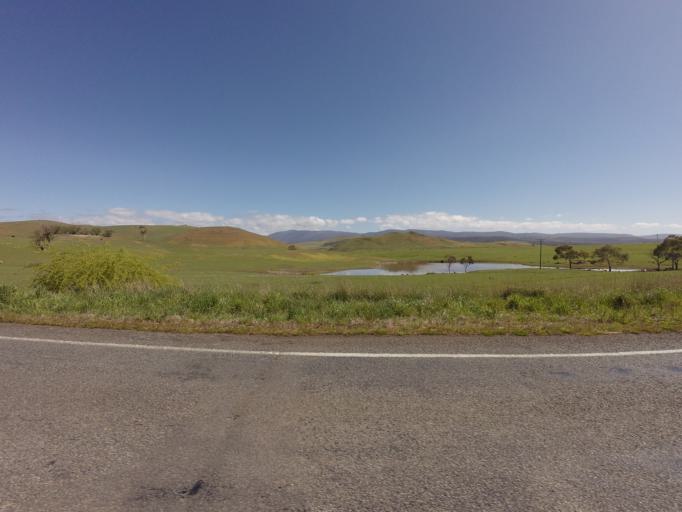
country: AU
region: Tasmania
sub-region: Derwent Valley
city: New Norfolk
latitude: -42.5437
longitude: 146.7752
